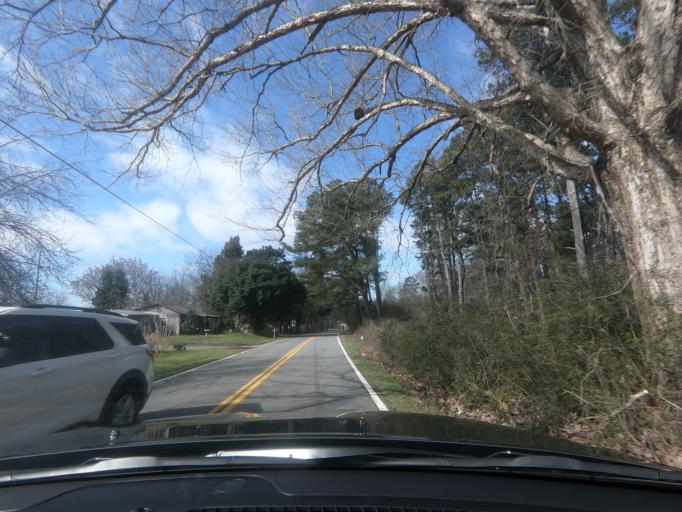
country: US
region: Georgia
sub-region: Cobb County
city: Acworth
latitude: 34.0633
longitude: -84.6452
